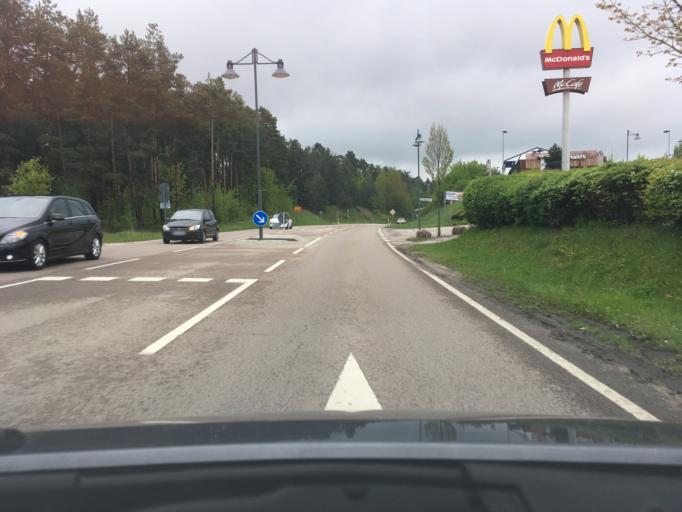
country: DE
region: Bavaria
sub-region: Upper Palatinate
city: Burglengenfeld
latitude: 49.1971
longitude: 12.0590
